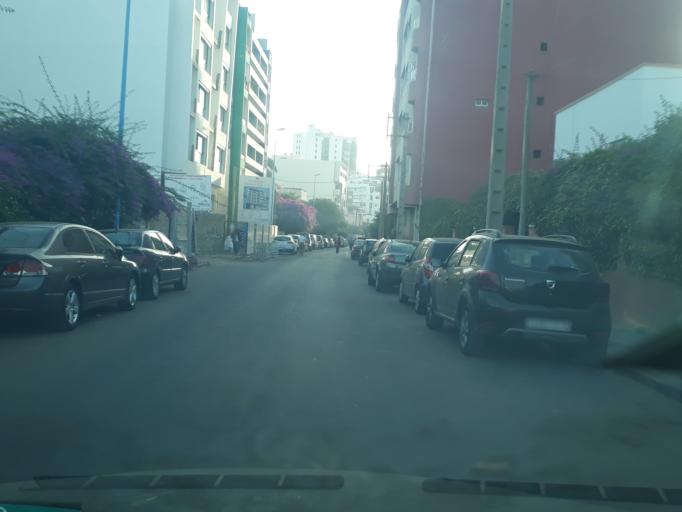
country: MA
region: Grand Casablanca
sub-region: Casablanca
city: Casablanca
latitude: 33.5793
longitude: -7.6296
